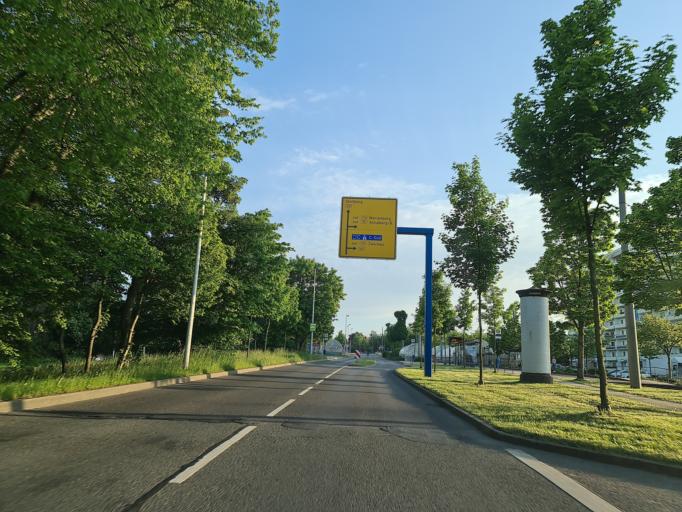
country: DE
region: Saxony
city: Neukirchen
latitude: 50.8042
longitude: 12.8877
